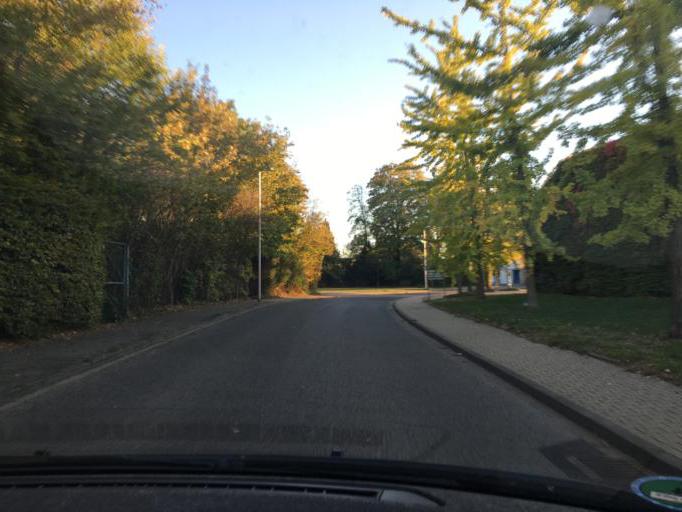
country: DE
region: North Rhine-Westphalia
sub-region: Regierungsbezirk Koln
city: Dueren
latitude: 50.8134
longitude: 6.4451
